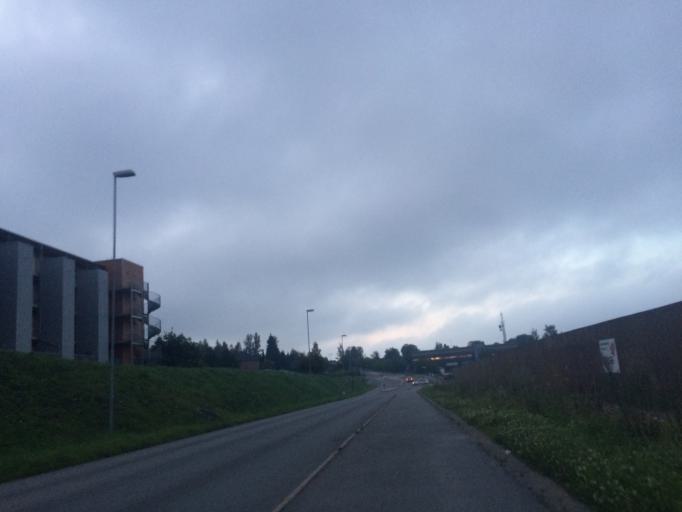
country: NO
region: Akershus
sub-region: Ski
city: Ski
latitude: 59.7169
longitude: 10.8319
